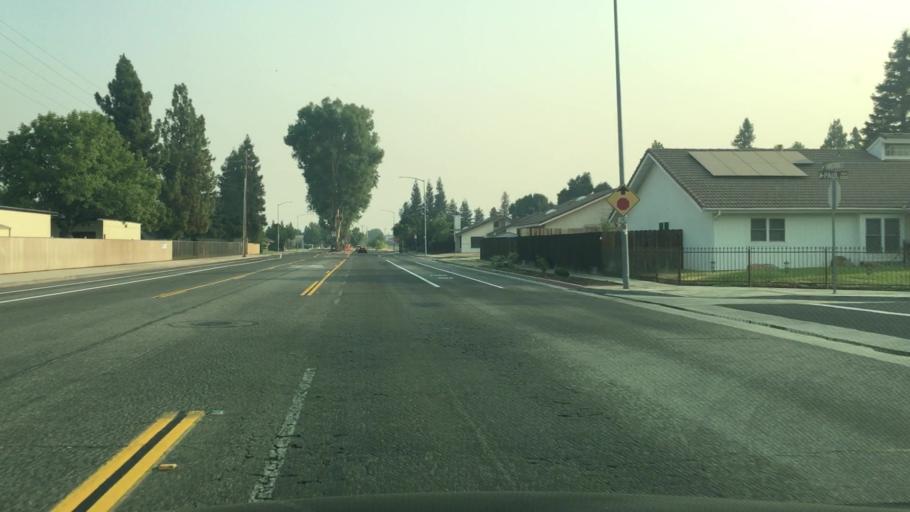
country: US
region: California
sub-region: Fresno County
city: Clovis
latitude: 36.8317
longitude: -119.6729
